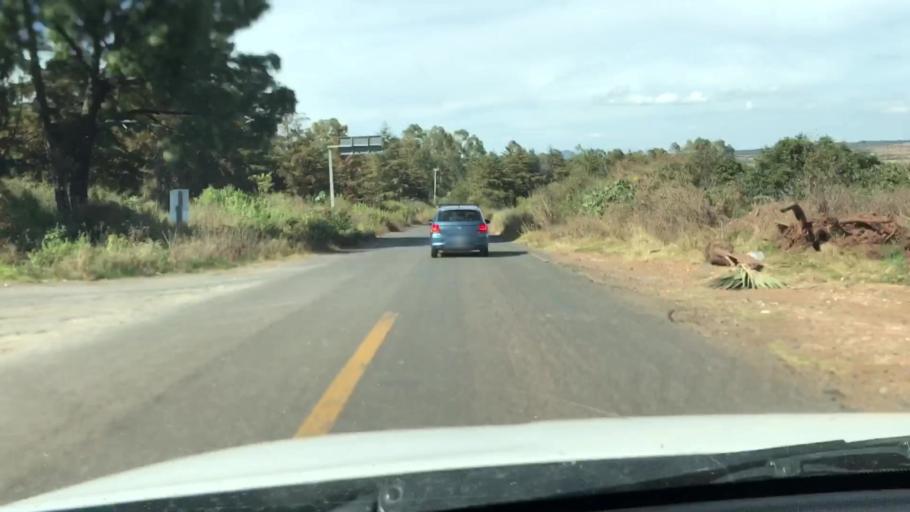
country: MX
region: Jalisco
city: Chiquilistlan
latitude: 20.1473
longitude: -103.7254
